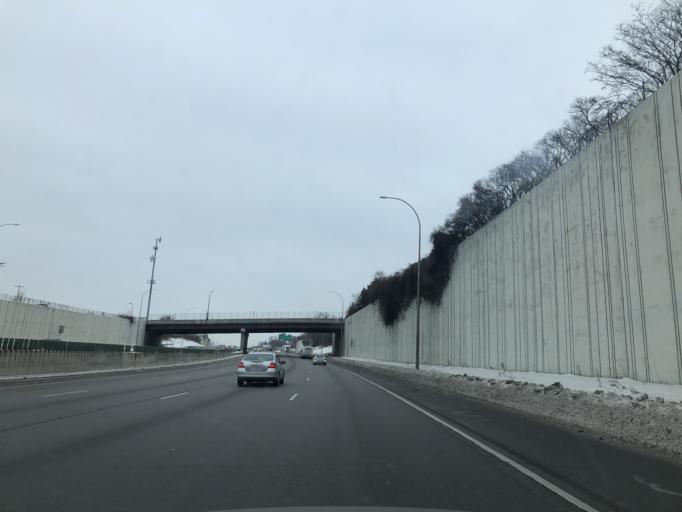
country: US
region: Minnesota
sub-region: Anoka County
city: Columbia Heights
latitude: 45.0309
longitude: -93.2876
